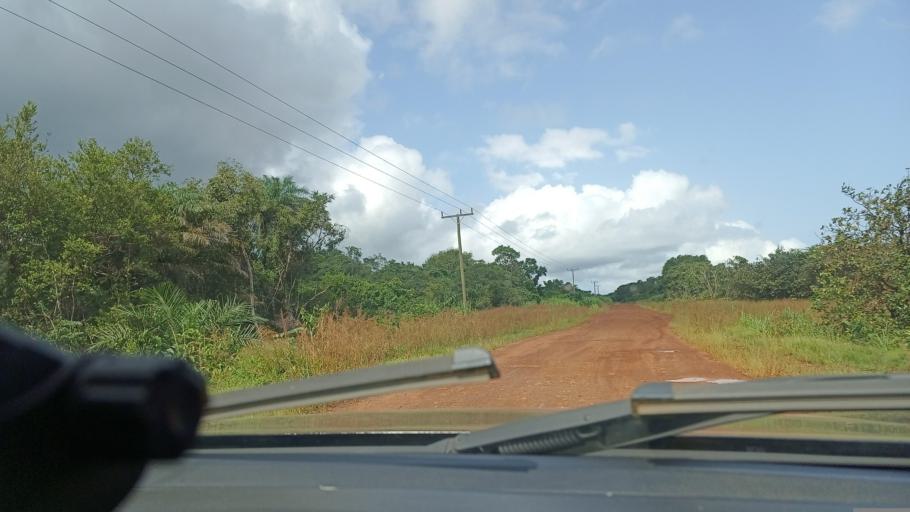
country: LR
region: Grand Cape Mount
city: Robertsport
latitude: 6.6897
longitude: -11.2591
